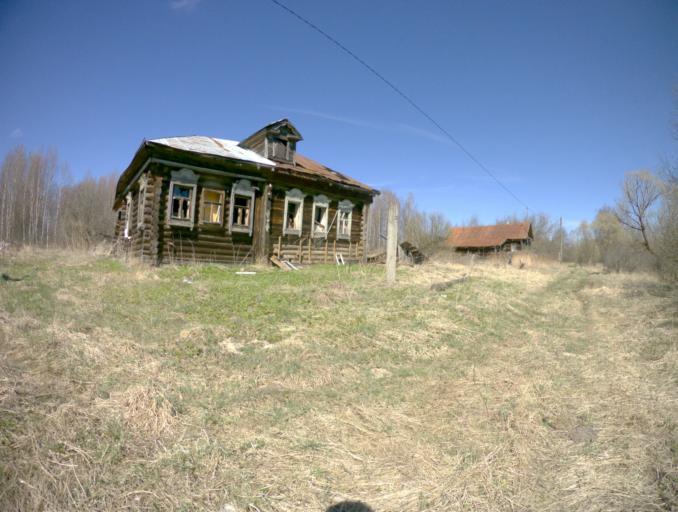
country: RU
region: Vladimir
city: Ivanishchi
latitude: 55.8640
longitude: 40.4345
